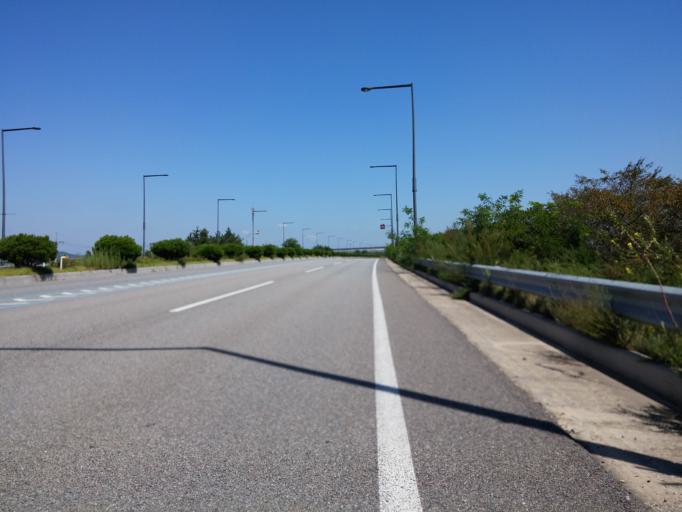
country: KR
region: Chungcheongbuk-do
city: Cheongju-si
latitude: 36.5953
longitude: 127.3315
